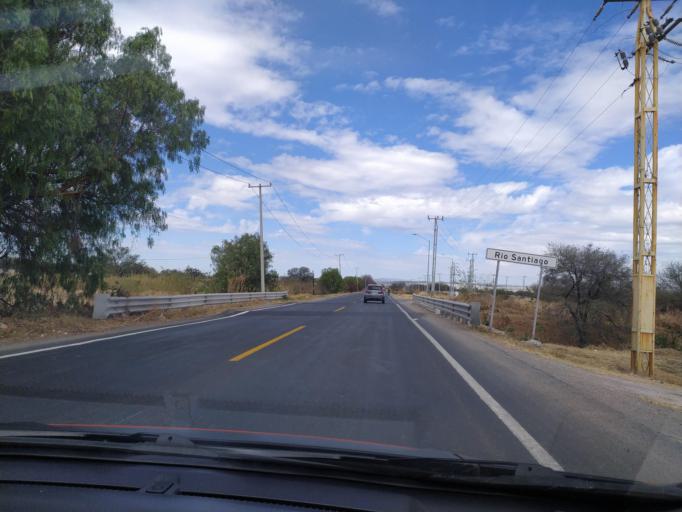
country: LA
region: Oudomxai
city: Muang La
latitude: 20.9975
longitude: 101.8333
